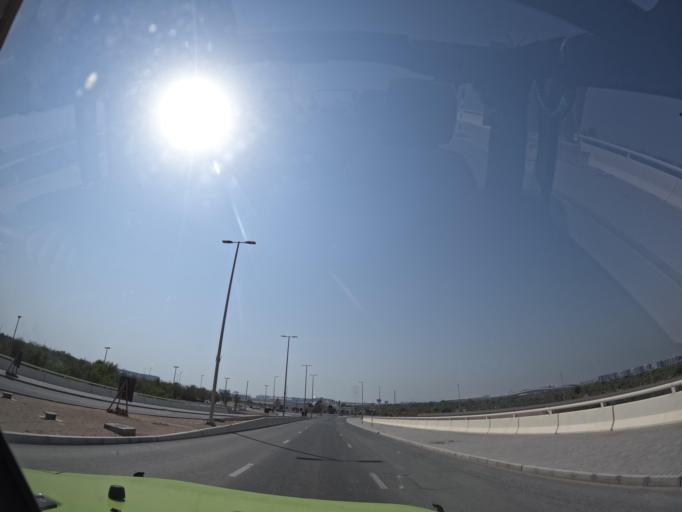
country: AE
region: Abu Dhabi
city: Abu Dhabi
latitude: 24.4647
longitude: 54.6268
